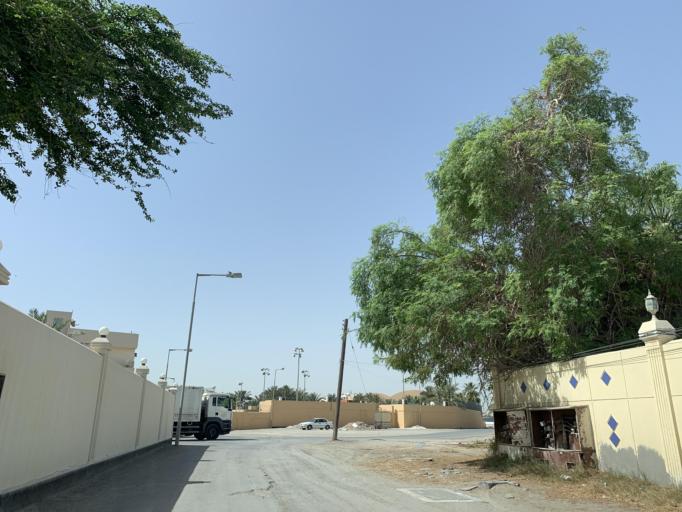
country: BH
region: Northern
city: Sitrah
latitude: 26.1472
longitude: 50.6008
